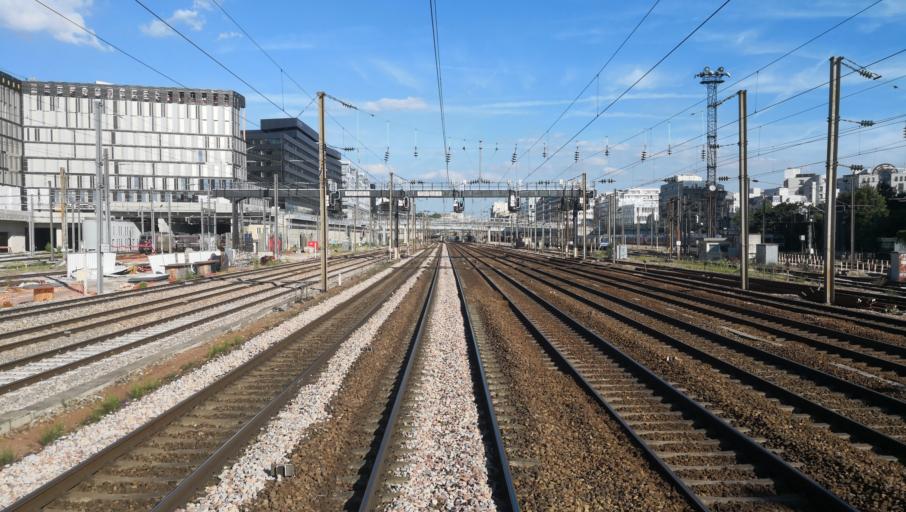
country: FR
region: Ile-de-France
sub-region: Departement des Hauts-de-Seine
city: Clichy
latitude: 48.8918
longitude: 2.3075
